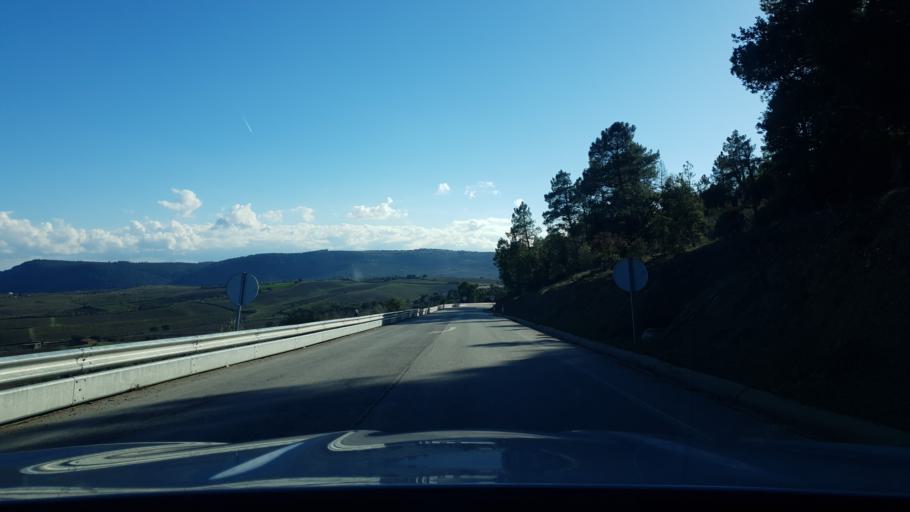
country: PT
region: Braganca
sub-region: Freixo de Espada A Cinta
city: Freixo de Espada a Cinta
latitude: 41.1018
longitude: -6.8293
